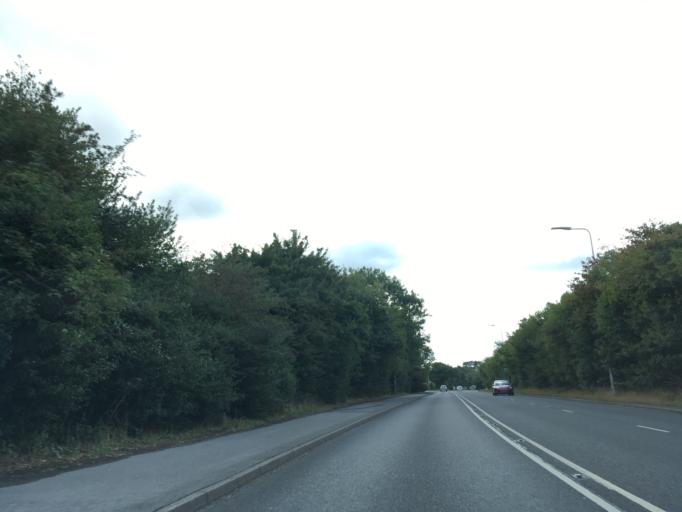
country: GB
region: England
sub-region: West Berkshire
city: Greenham
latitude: 51.3828
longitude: -1.3202
